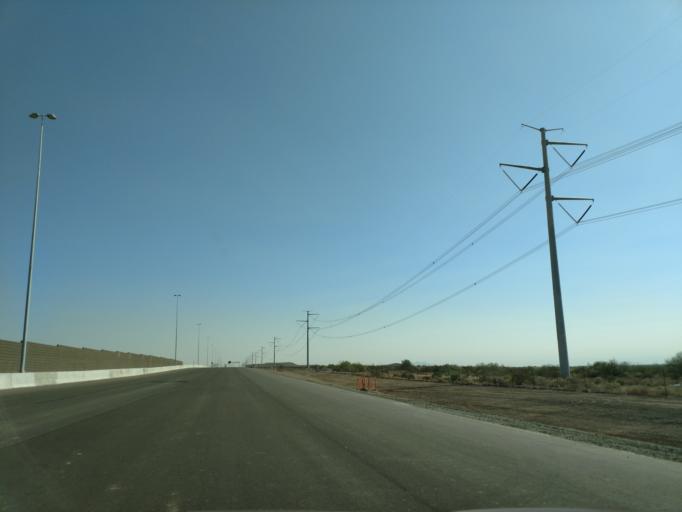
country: US
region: Arizona
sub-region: Maricopa County
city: Laveen
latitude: 33.2911
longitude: -112.1197
